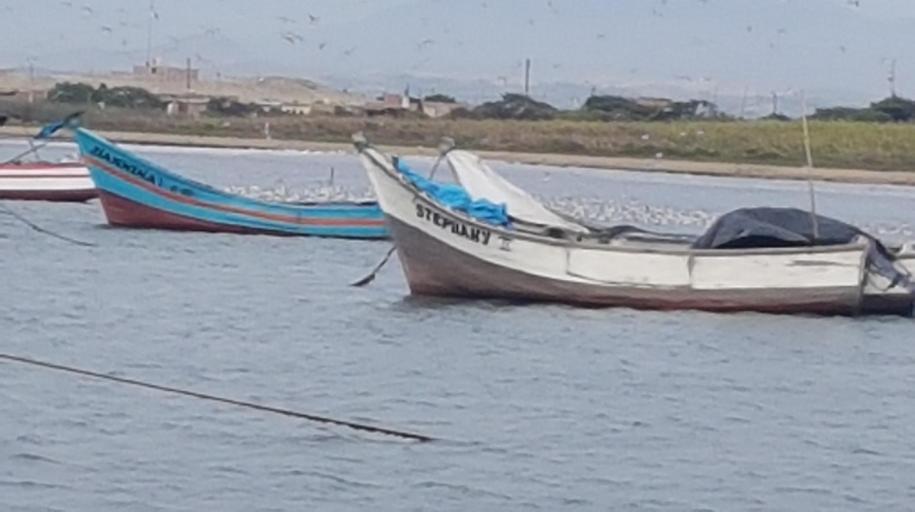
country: PE
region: Ancash
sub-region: Provincia de Santa
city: Puerto Santa
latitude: -8.9902
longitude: -78.6524
